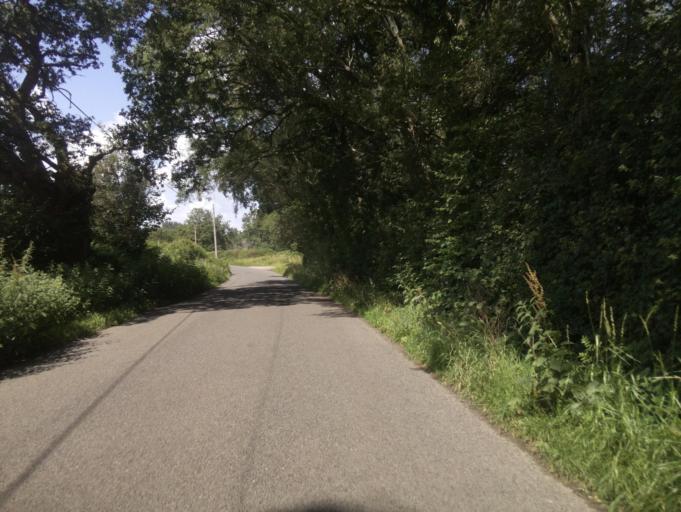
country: GB
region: England
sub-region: West Berkshire
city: Greenham
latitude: 51.3530
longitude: -1.2816
